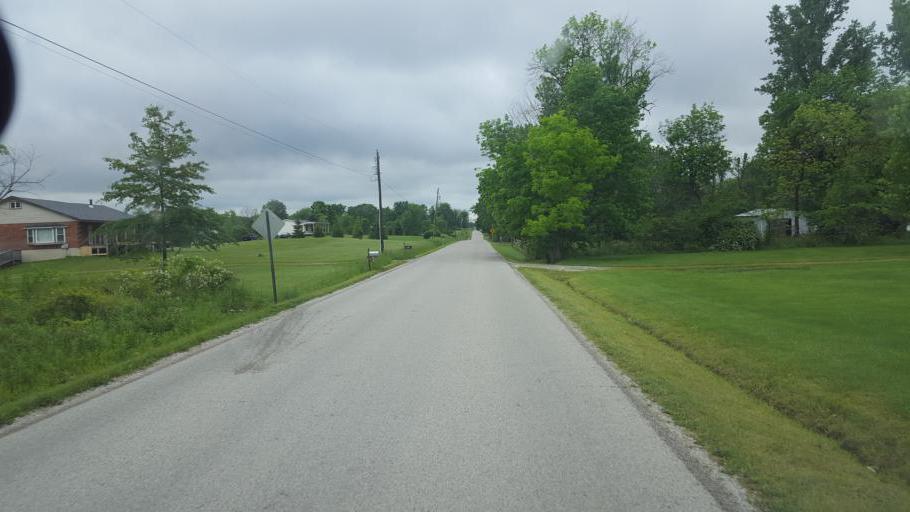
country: US
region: Ohio
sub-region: Morrow County
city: Cardington
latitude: 40.4496
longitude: -82.8076
